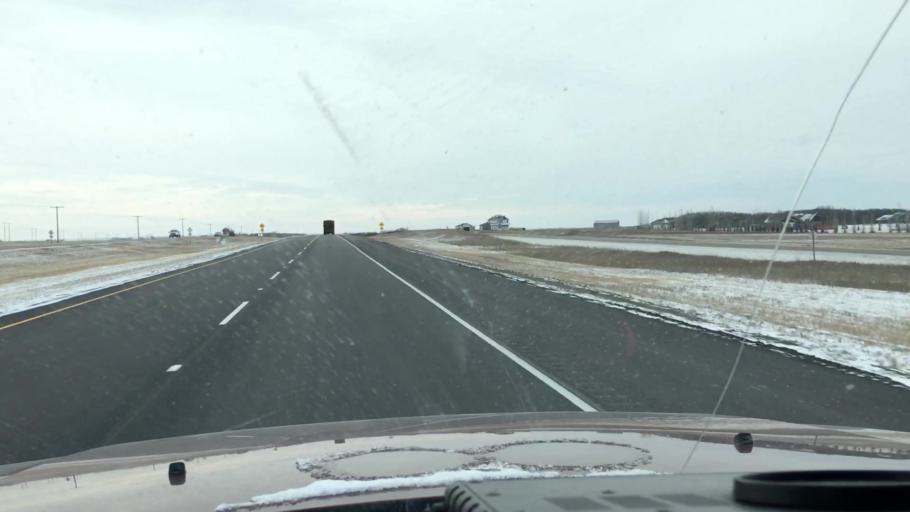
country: CA
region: Saskatchewan
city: Saskatoon
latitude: 51.9320
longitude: -106.5363
